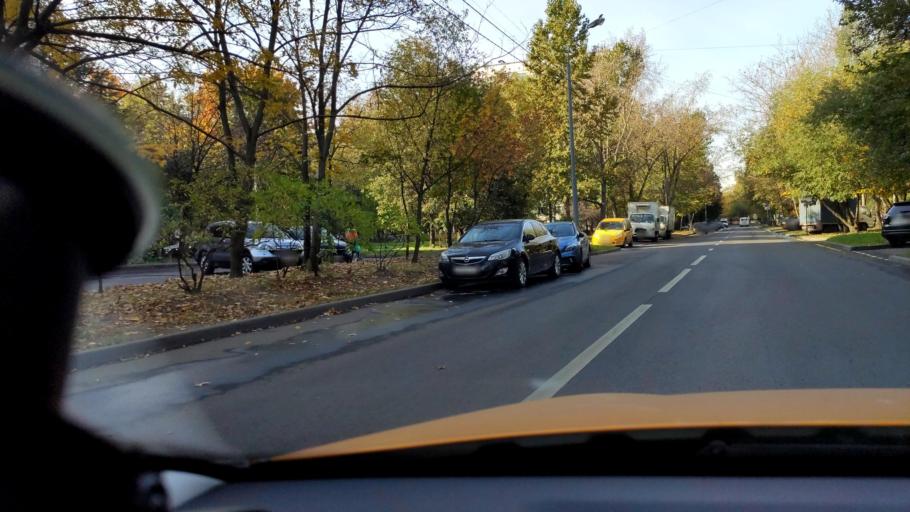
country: RU
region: Moscow
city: Altuf'yevskiy
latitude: 55.8799
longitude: 37.5751
